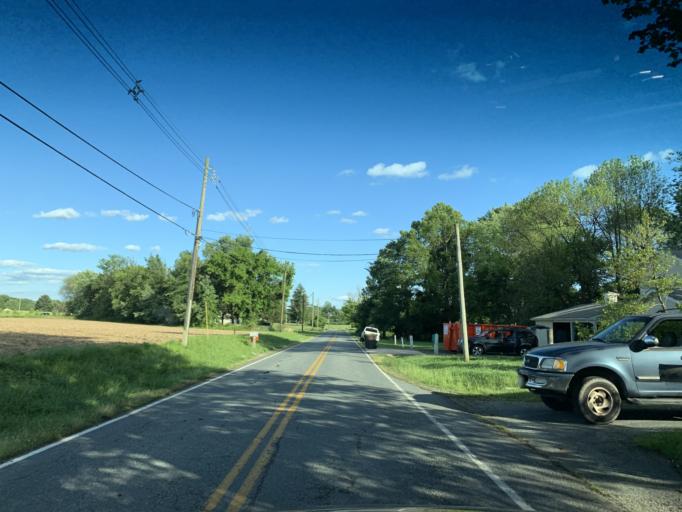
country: US
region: Maryland
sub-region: Cecil County
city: North East
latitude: 39.6747
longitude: -75.9640
